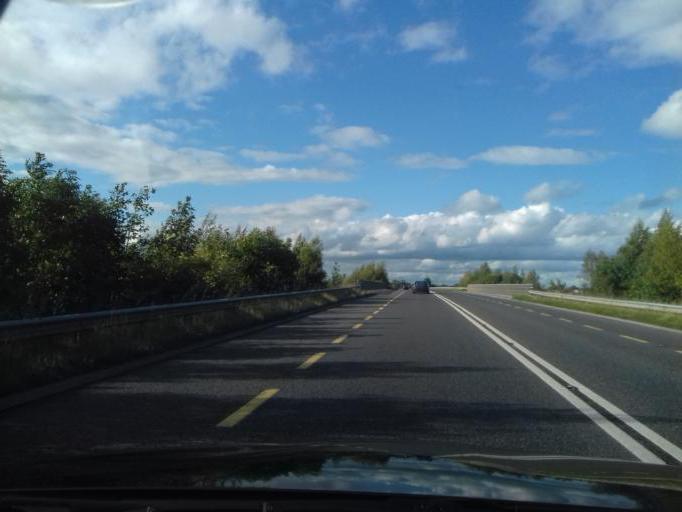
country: IE
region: Leinster
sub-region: Uibh Fhaili
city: Tullamore
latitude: 53.2788
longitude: -7.4687
